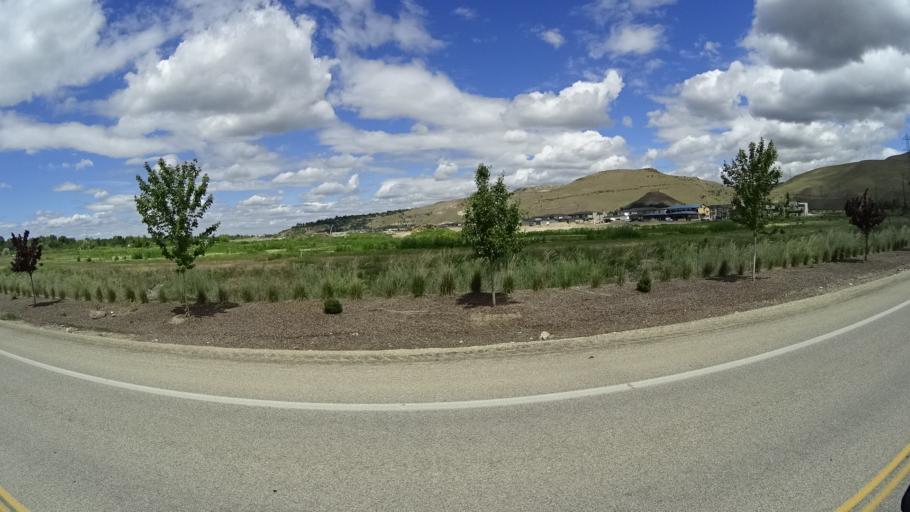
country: US
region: Idaho
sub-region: Ada County
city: Boise
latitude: 43.5696
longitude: -116.1275
